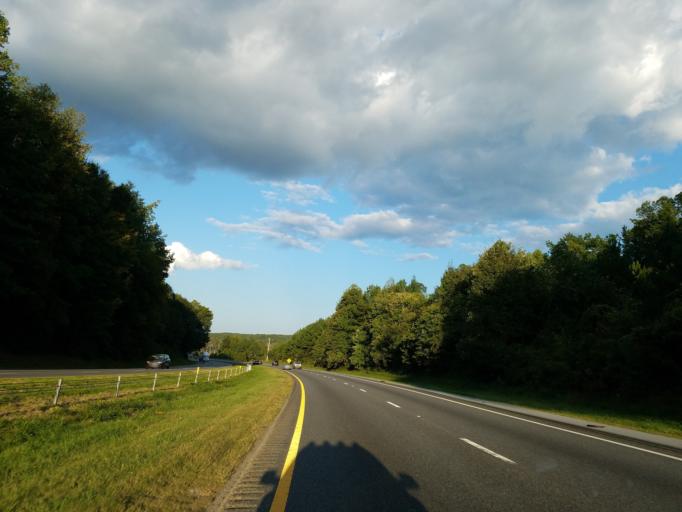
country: US
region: South Carolina
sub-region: Cherokee County
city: East Gaffney
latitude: 35.1104
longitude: -81.5885
